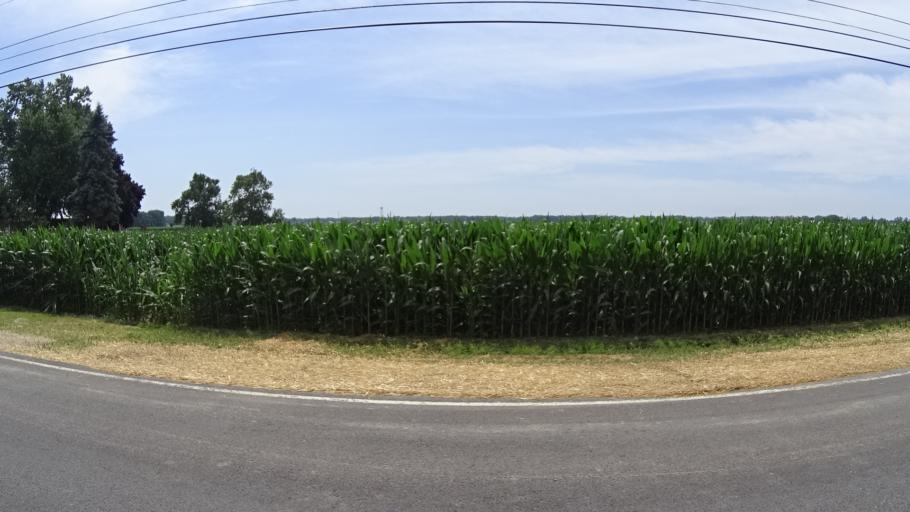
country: US
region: Ohio
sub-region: Erie County
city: Sandusky
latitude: 41.4135
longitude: -82.7717
